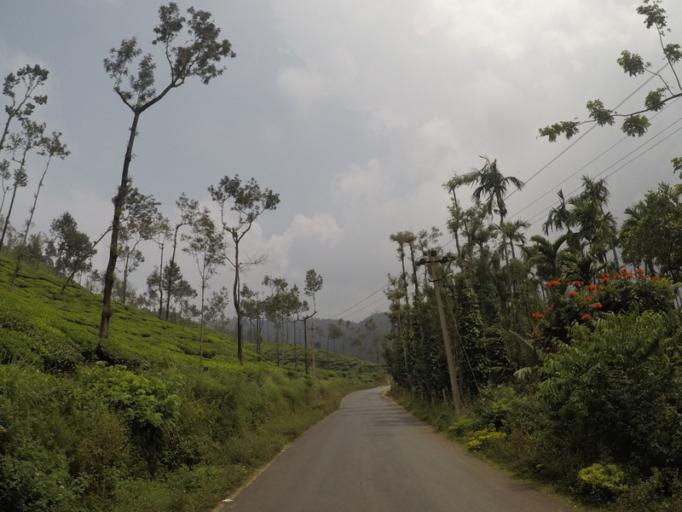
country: IN
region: Karnataka
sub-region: Chikmagalur
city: Mudigere
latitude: 13.1677
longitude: 75.4587
